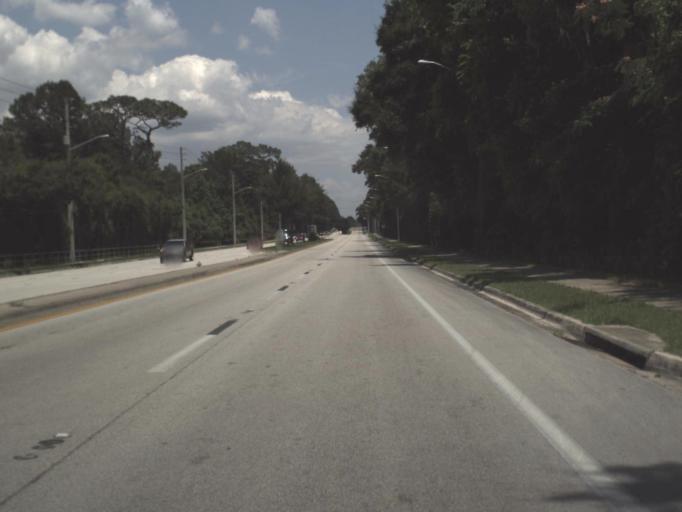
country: US
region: Florida
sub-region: Alachua County
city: Alachua
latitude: 29.6599
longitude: -82.4677
